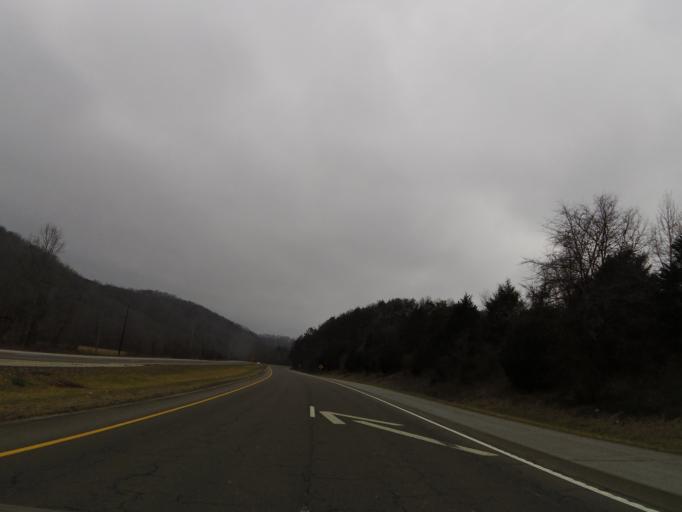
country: US
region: Tennessee
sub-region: Anderson County
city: Rocky Top
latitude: 36.1677
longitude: -84.1442
